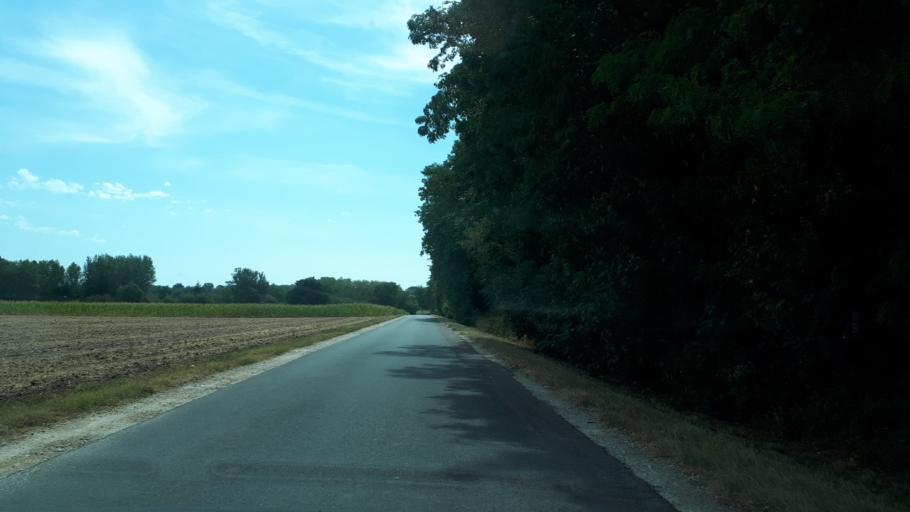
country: FR
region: Centre
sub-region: Departement du Loir-et-Cher
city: Chitenay
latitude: 47.4419
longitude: 1.3505
